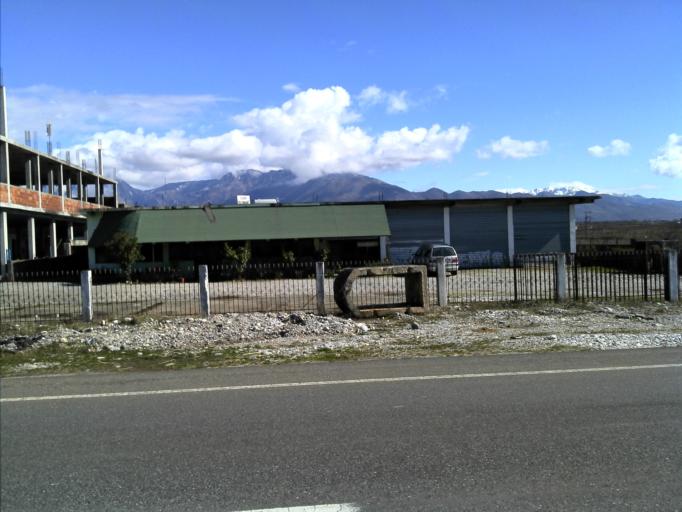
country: AL
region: Shkoder
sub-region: Rrethi i Malesia e Madhe
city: Grude-Fushe
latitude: 42.1624
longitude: 19.4701
